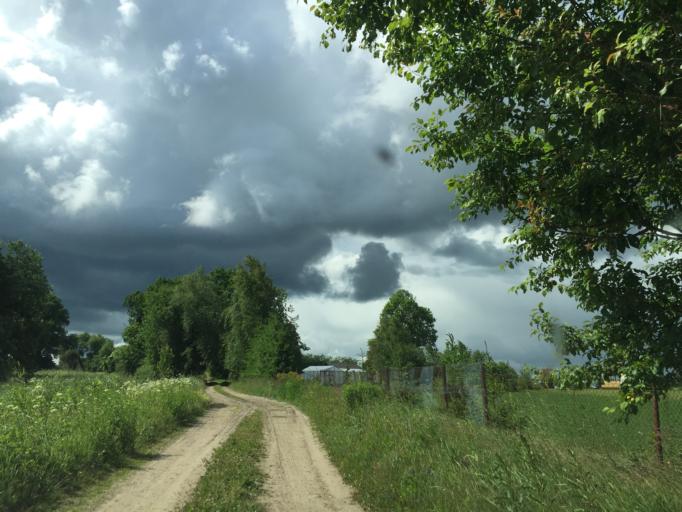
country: LV
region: Lecava
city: Iecava
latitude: 56.6089
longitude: 24.2021
